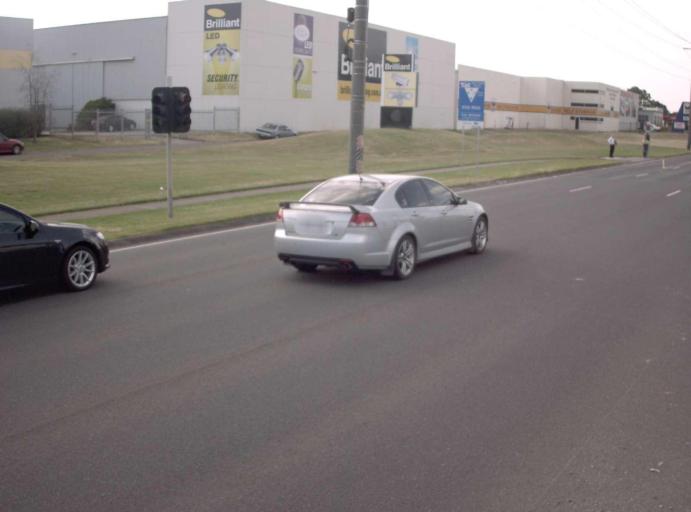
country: AU
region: Victoria
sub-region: Knox
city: Scoresby
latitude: -37.9107
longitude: 145.2364
